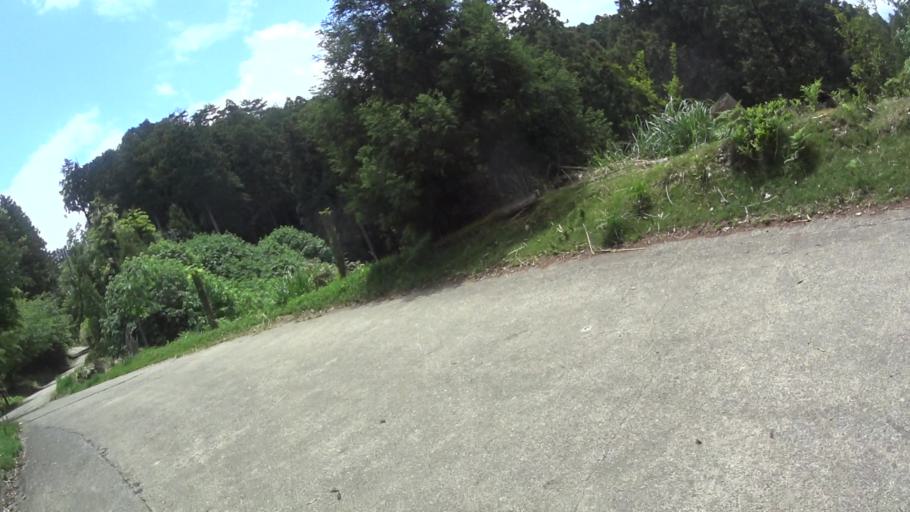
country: JP
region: Nara
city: Yoshino-cho
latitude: 34.3528
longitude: 135.8734
